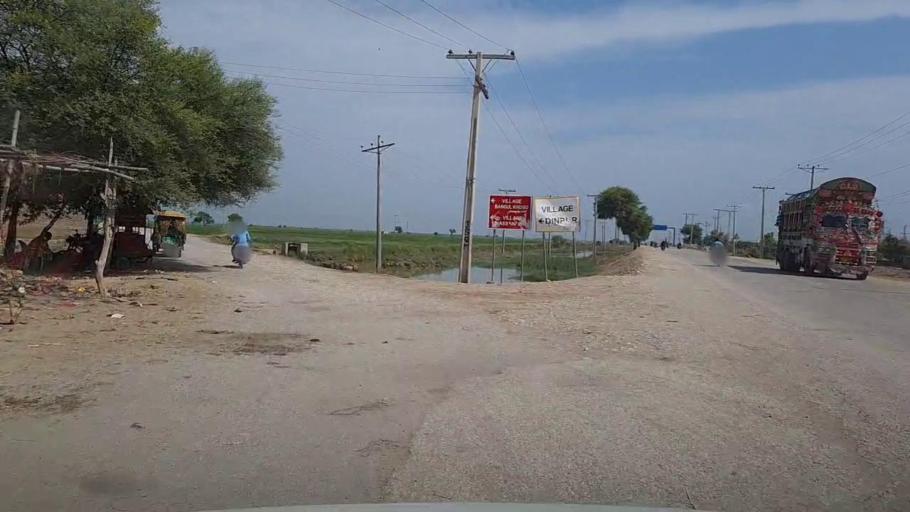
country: PK
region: Sindh
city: Thul
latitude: 28.2304
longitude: 68.7914
